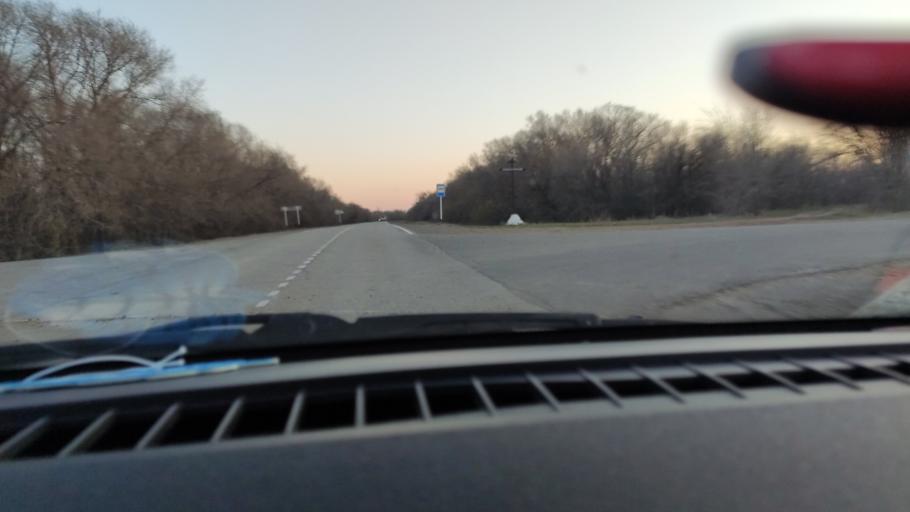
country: RU
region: Saratov
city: Privolzhskiy
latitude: 51.2447
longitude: 45.9342
